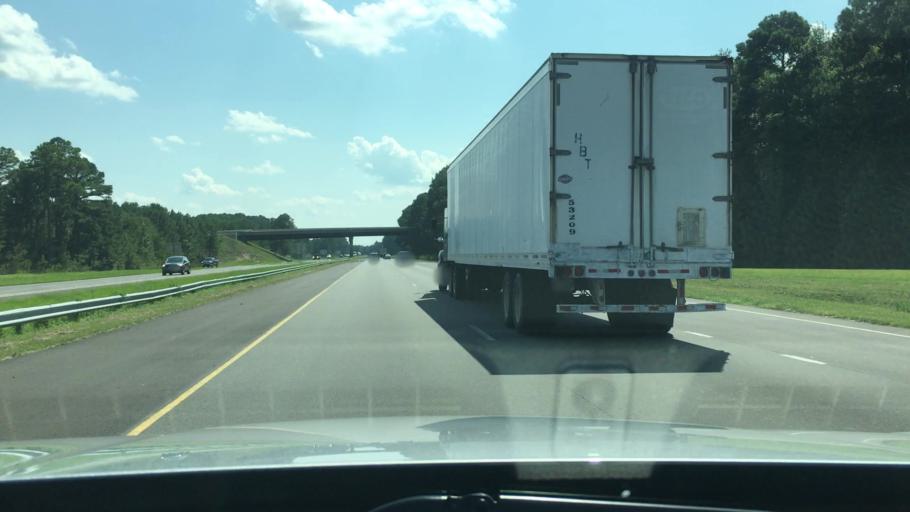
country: US
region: North Carolina
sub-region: Cumberland County
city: Eastover
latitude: 35.1222
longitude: -78.7555
